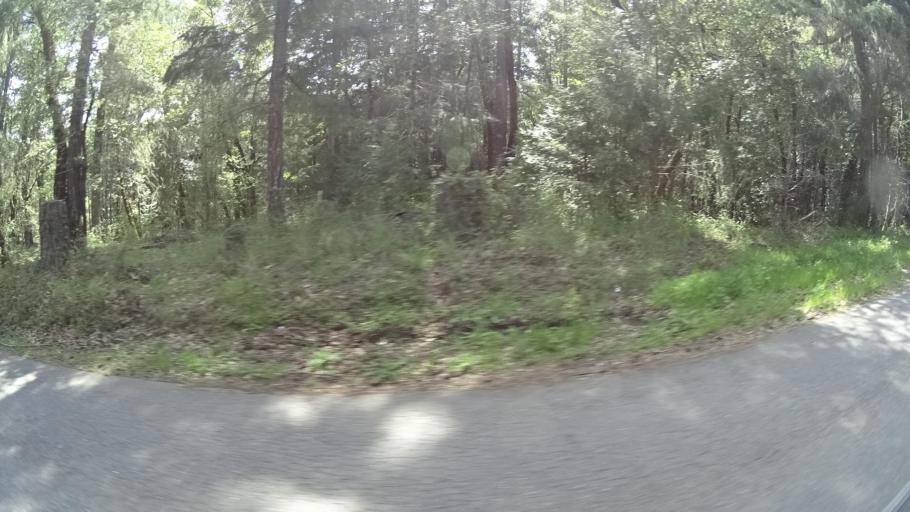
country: US
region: California
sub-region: Humboldt County
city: Redway
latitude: 40.3895
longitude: -123.7431
